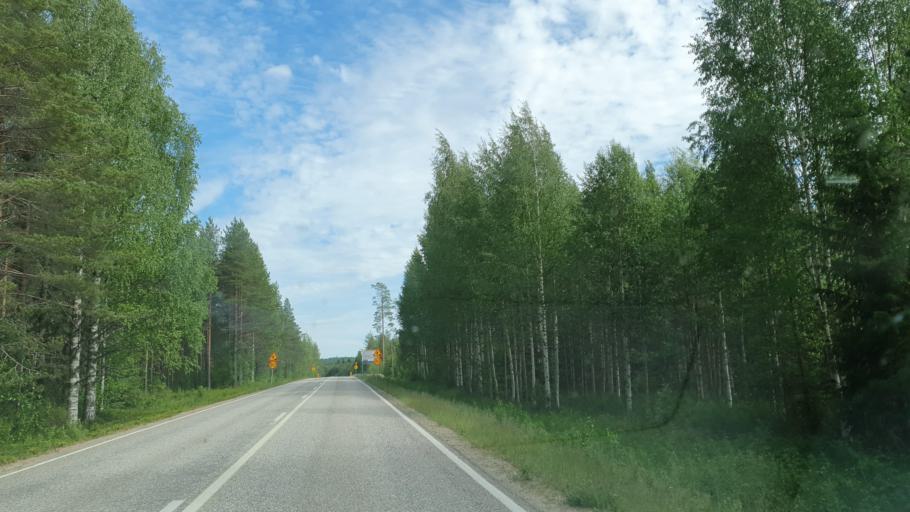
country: FI
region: Kainuu
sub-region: Kehys-Kainuu
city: Suomussalmi
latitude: 64.5669
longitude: 28.8785
